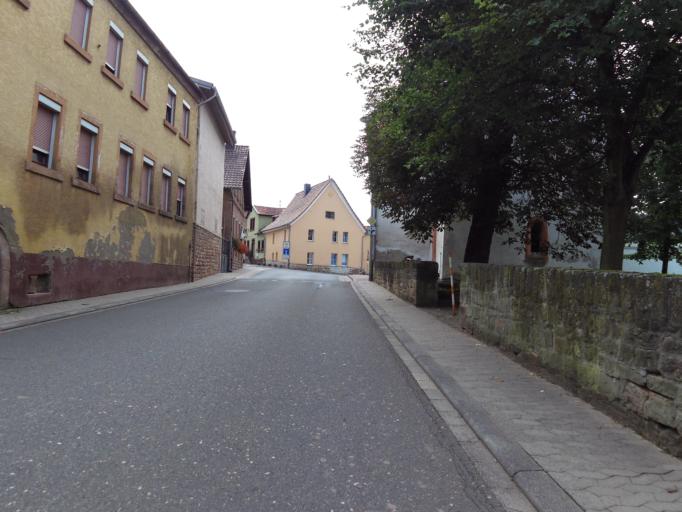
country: DE
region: Rheinland-Pfalz
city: Hochstatten
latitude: 49.7650
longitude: 7.8323
